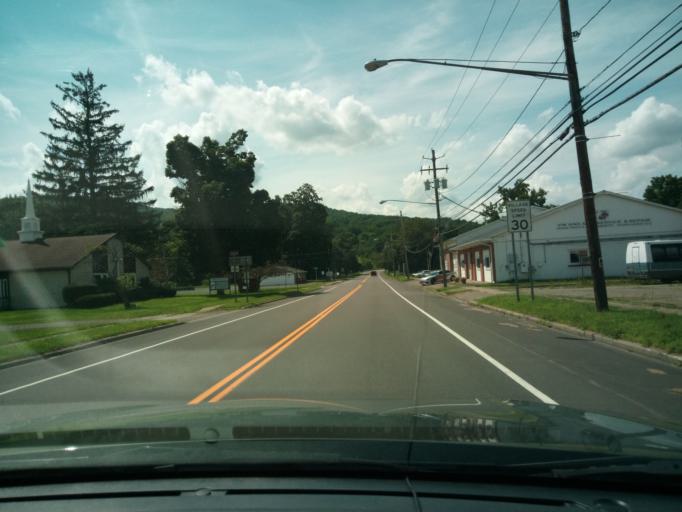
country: US
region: New York
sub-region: Chemung County
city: Southport
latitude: 42.0164
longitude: -76.7277
